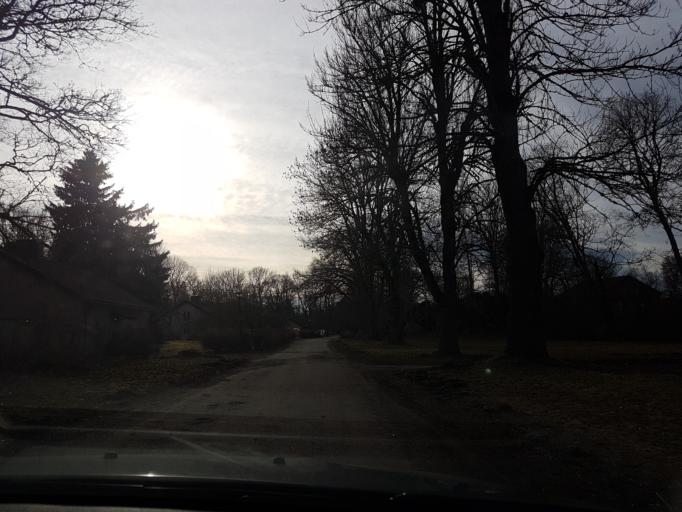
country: SE
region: Stockholm
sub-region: Norrtalje Kommun
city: Rimbo
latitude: 59.7386
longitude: 18.4954
